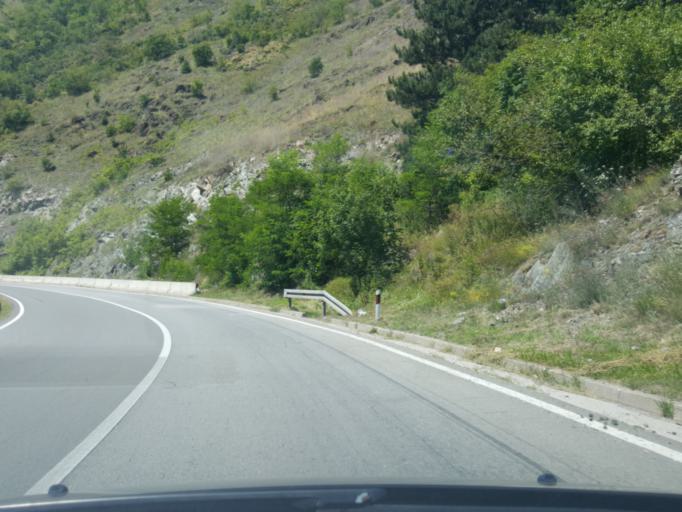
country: RS
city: Prislonica
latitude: 43.9885
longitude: 20.4187
